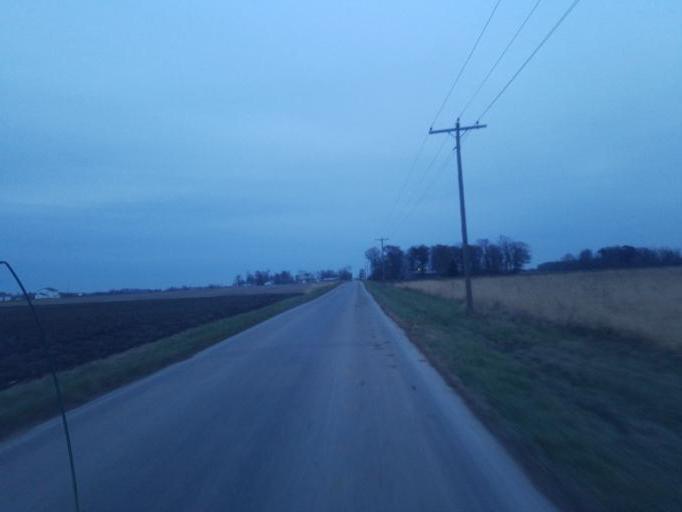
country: US
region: Indiana
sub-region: Adams County
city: Berne
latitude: 40.7314
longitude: -84.9235
